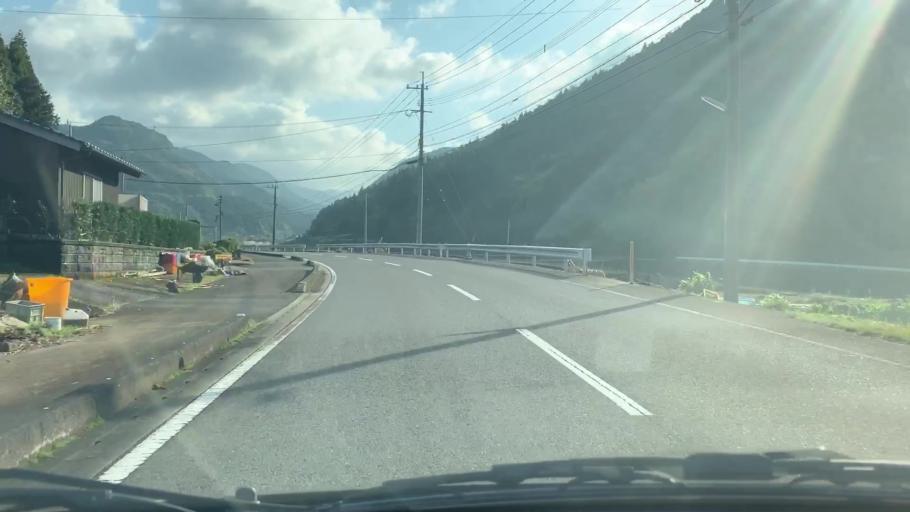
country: JP
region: Saga Prefecture
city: Kashima
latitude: 33.0602
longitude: 130.0699
